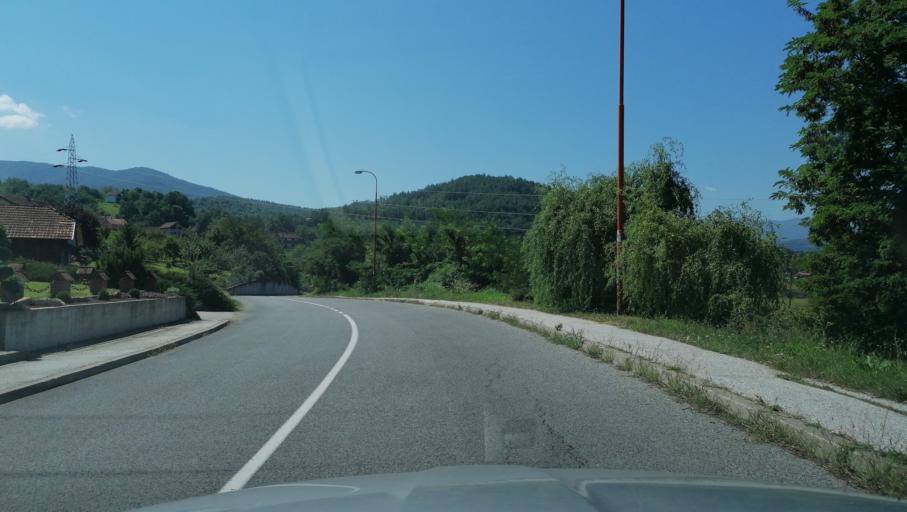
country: RS
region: Central Serbia
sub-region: Raski Okrug
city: Kraljevo
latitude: 43.6915
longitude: 20.6306
